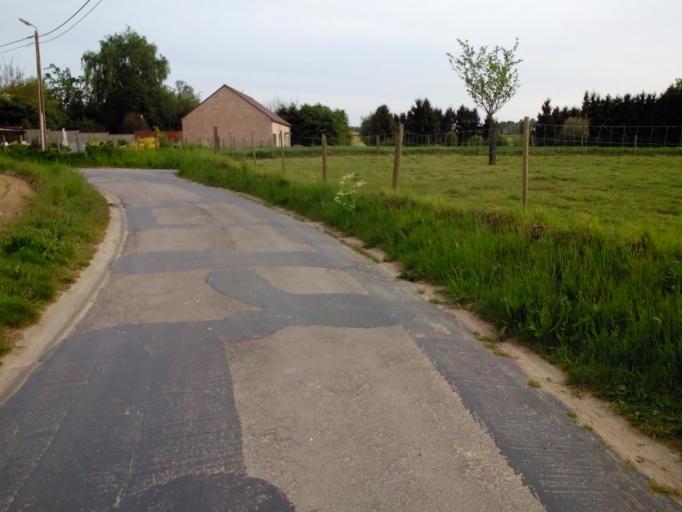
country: BE
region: Flanders
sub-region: Provincie Vlaams-Brabant
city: Bierbeek
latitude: 50.8415
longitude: 4.7238
